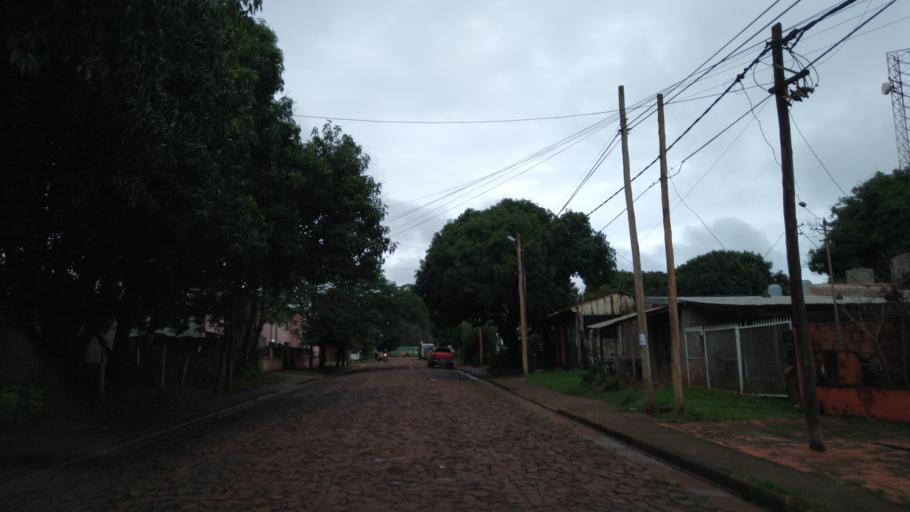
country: AR
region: Misiones
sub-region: Departamento de Capital
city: Posadas
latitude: -27.3995
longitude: -55.9305
